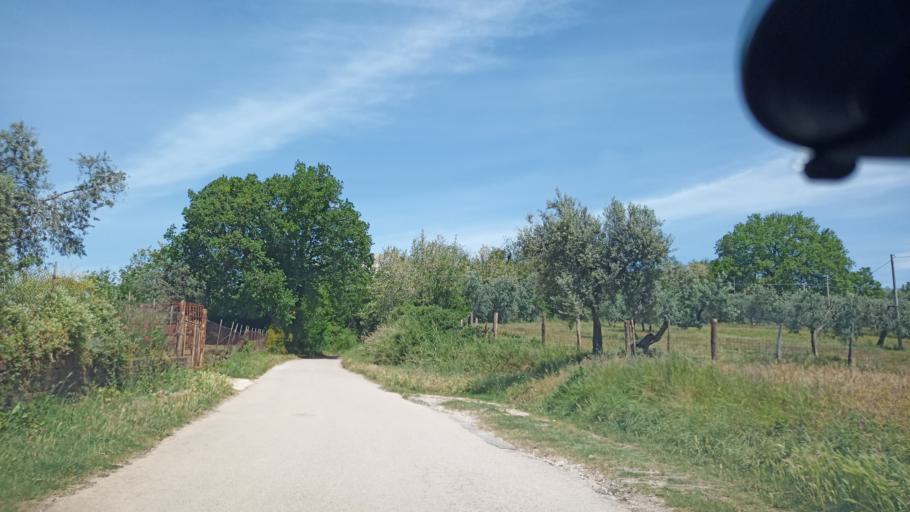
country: IT
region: Latium
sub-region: Provincia di Rieti
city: Torri in Sabina
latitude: 42.3483
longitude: 12.6201
